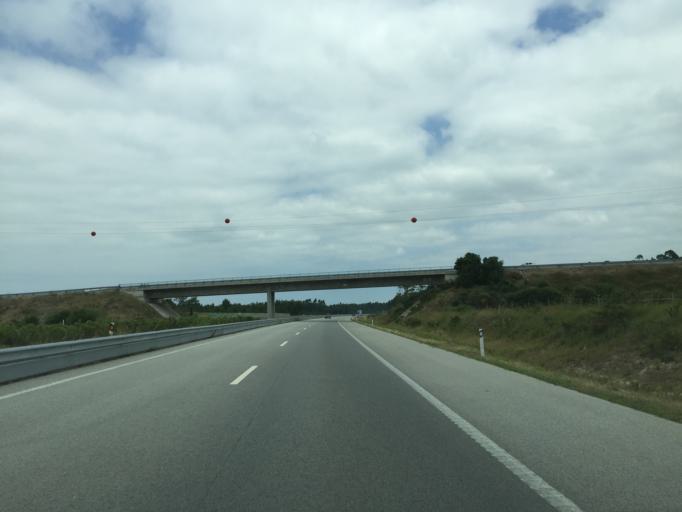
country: PT
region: Coimbra
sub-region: Figueira da Foz
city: Alhadas
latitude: 40.1896
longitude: -8.8119
